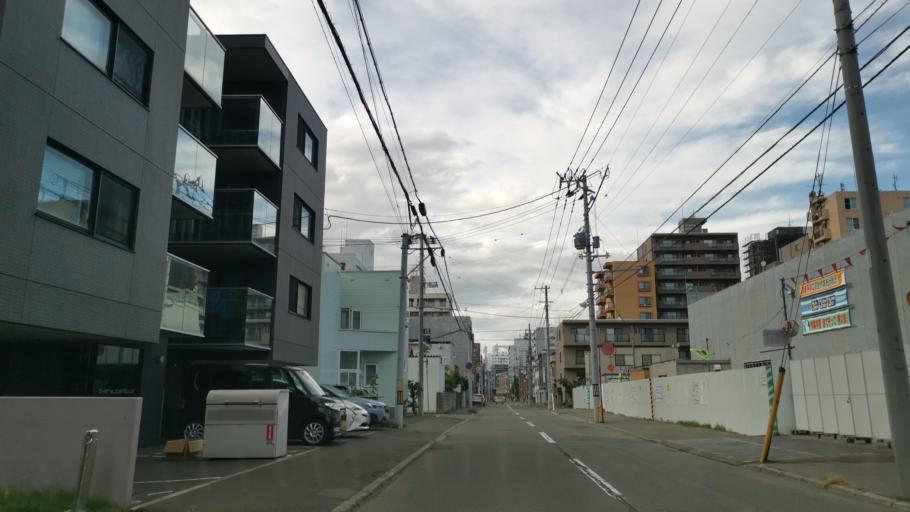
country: JP
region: Hokkaido
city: Sapporo
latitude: 43.0503
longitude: 141.3369
